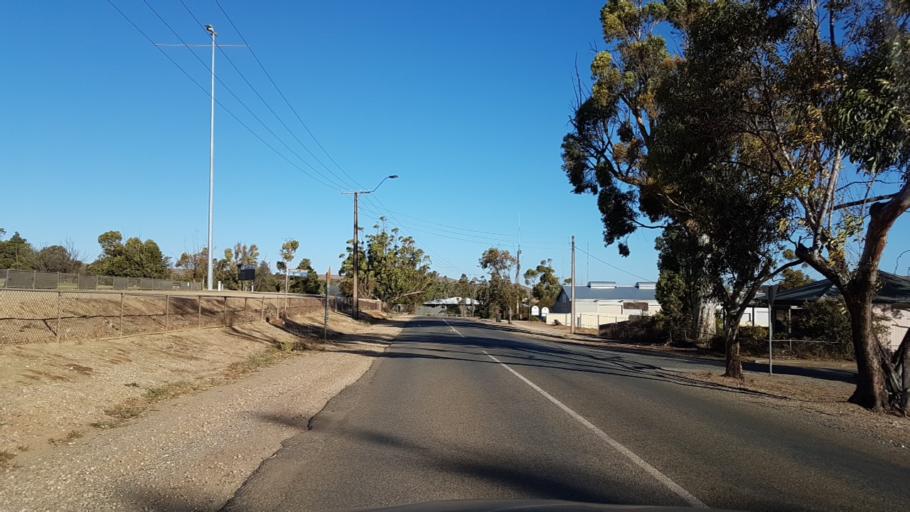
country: AU
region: South Australia
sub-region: Clare and Gilbert Valleys
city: Clare
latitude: -33.6766
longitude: 138.9402
